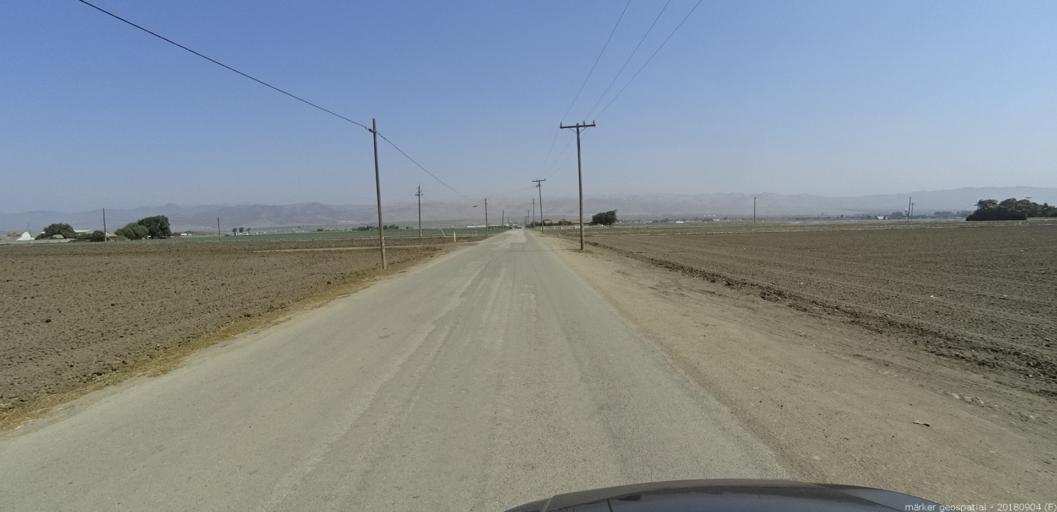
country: US
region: California
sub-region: Monterey County
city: Gonzales
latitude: 36.5130
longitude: -121.4684
